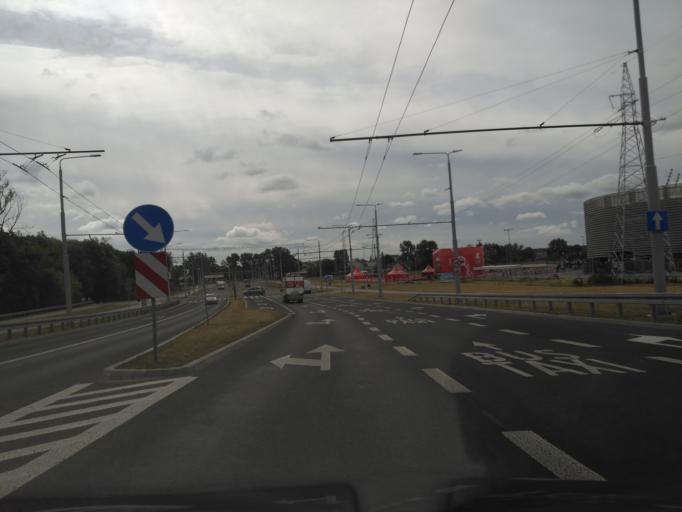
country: PL
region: Lublin Voivodeship
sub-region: Powiat lubelski
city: Lublin
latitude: 51.2346
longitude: 22.5576
